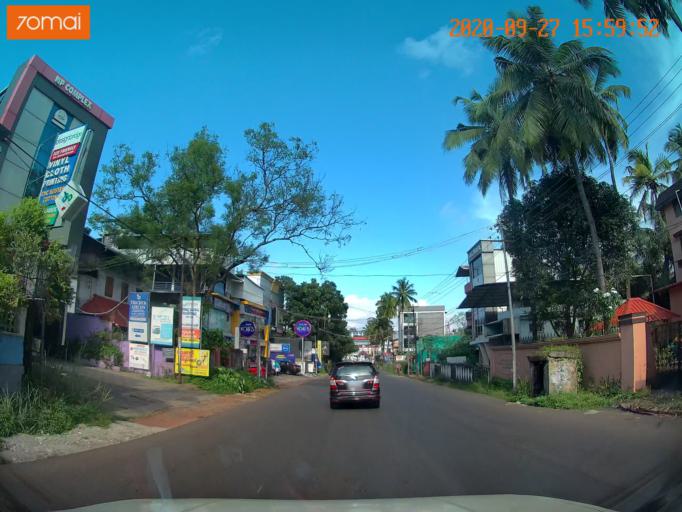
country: IN
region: Kerala
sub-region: Thrissur District
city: Trichur
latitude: 10.5207
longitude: 76.1973
